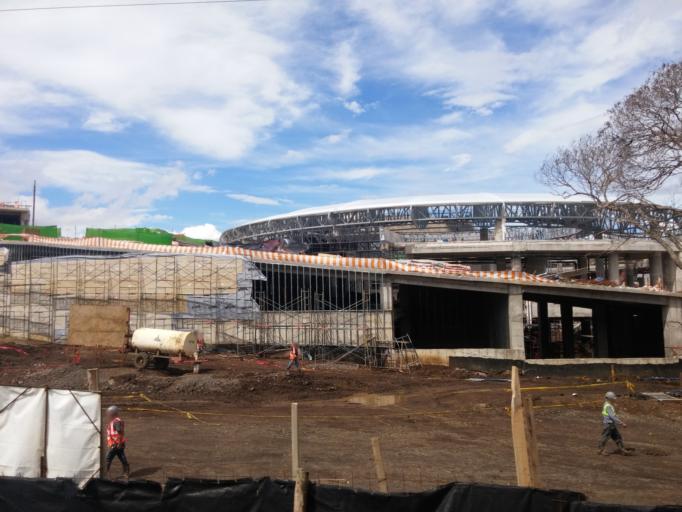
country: CR
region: Heredia
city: San Francisco
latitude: 9.9952
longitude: -84.1308
